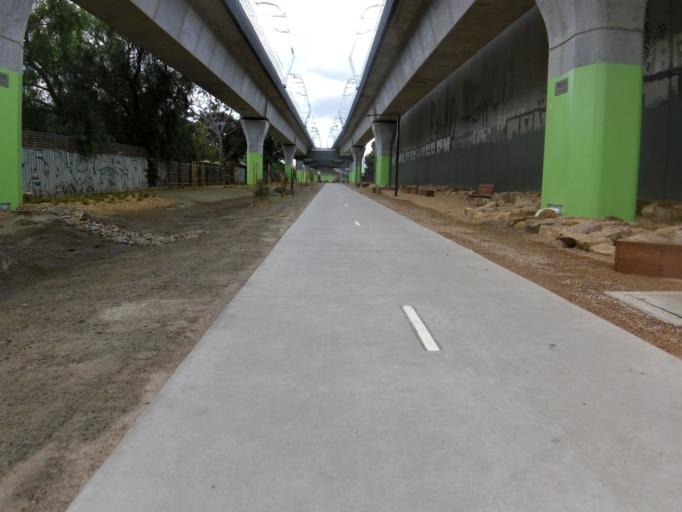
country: AU
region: Victoria
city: Glen Huntly
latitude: -37.8839
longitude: 145.0533
